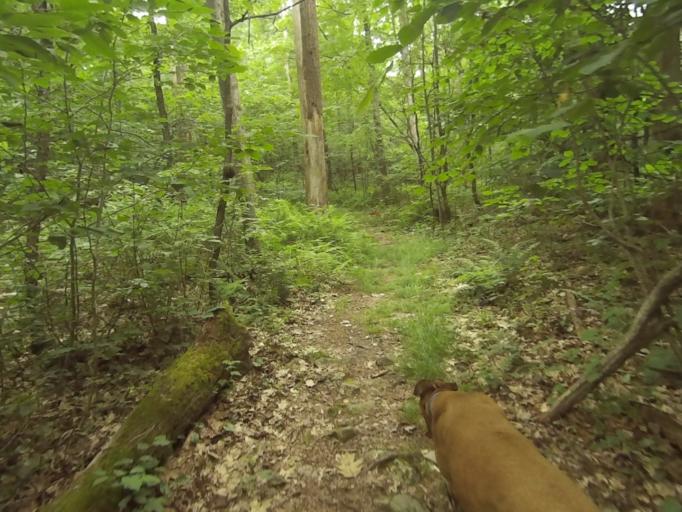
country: US
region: Pennsylvania
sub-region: Centre County
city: Stormstown
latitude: 40.9181
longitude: -78.0692
